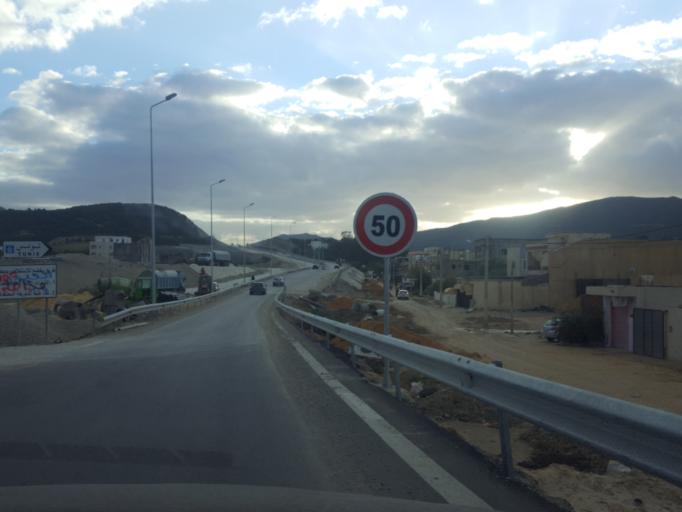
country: TN
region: Tunis
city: Hammam-Lif
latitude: 36.7004
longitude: 10.4026
